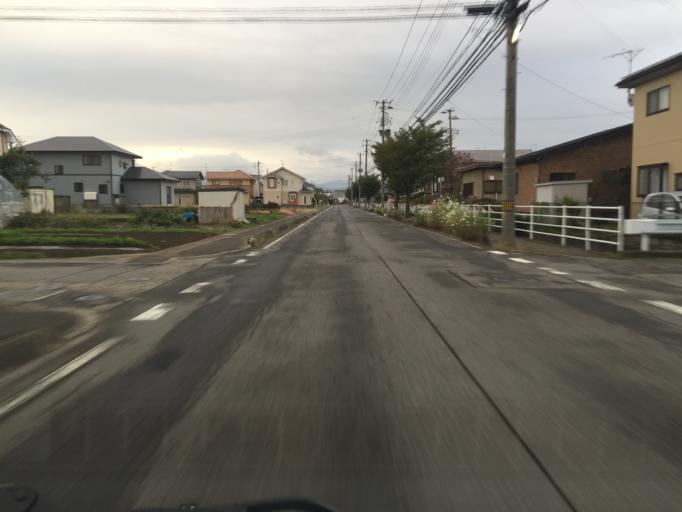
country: JP
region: Fukushima
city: Kitakata
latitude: 37.5195
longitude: 139.8749
